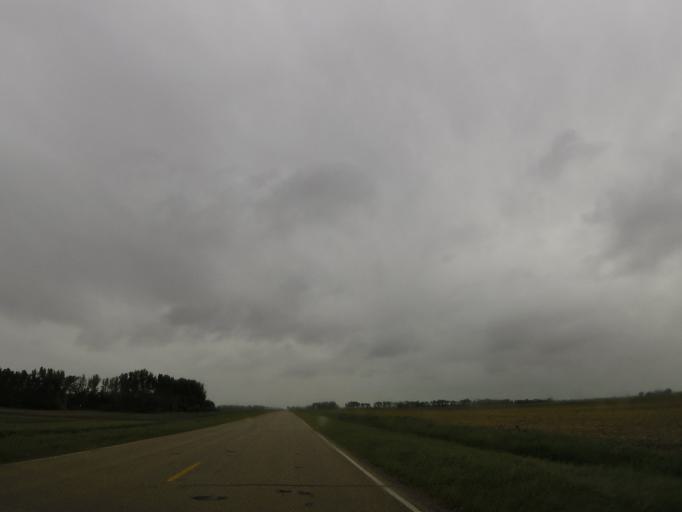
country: US
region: North Dakota
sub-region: Walsh County
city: Grafton
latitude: 48.5692
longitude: -97.2997
